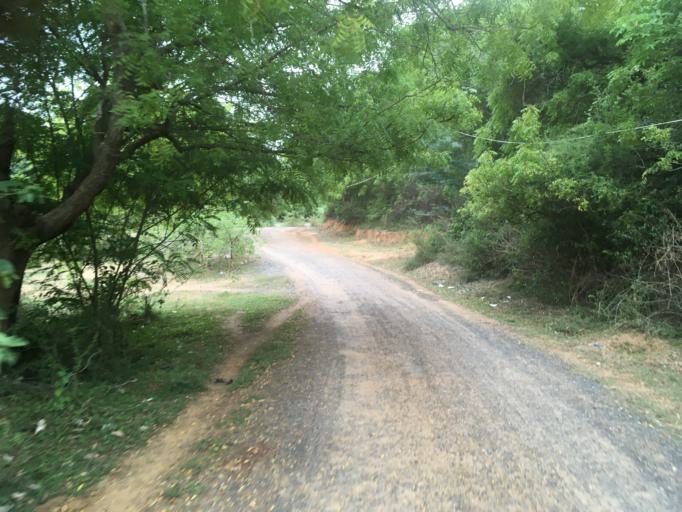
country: IN
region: Tamil Nadu
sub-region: Villupuram
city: Auroville
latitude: 12.0122
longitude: 79.8036
